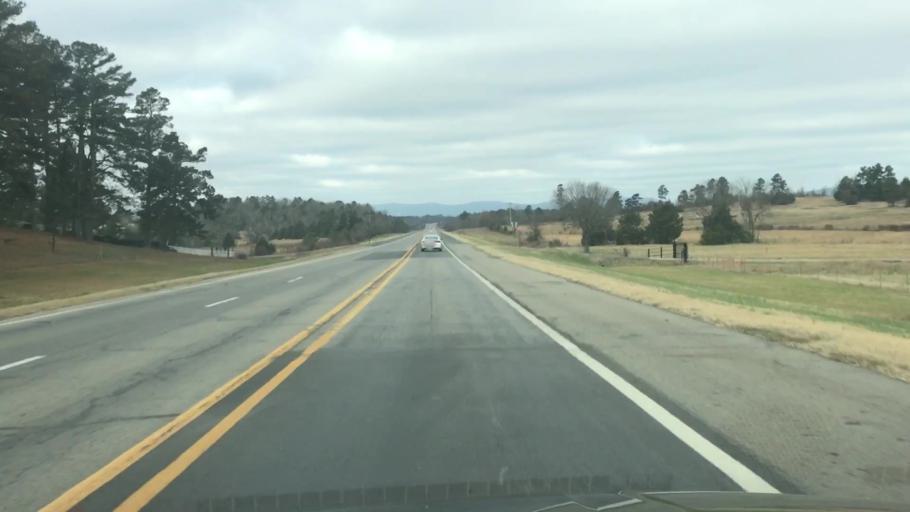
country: US
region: Arkansas
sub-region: Scott County
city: Waldron
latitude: 34.8691
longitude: -94.0806
